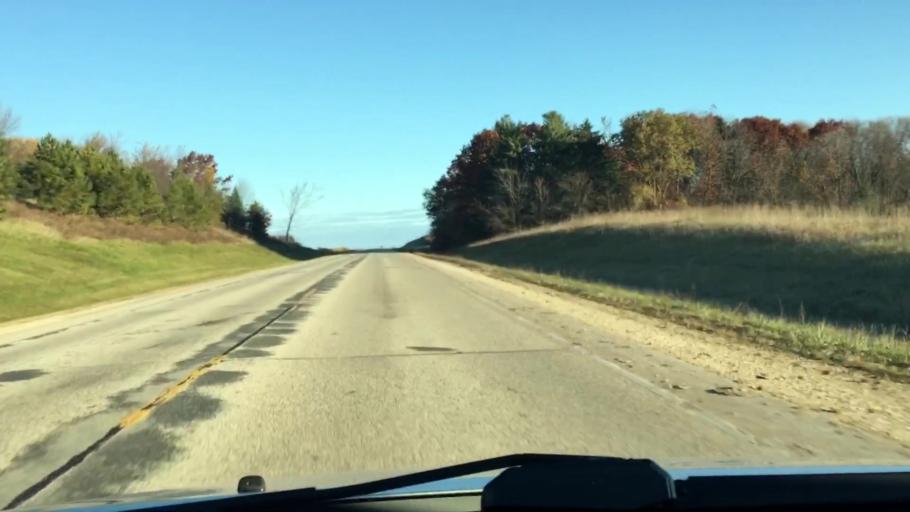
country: US
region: Wisconsin
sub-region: Dodge County
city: Theresa
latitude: 43.4624
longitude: -88.4500
